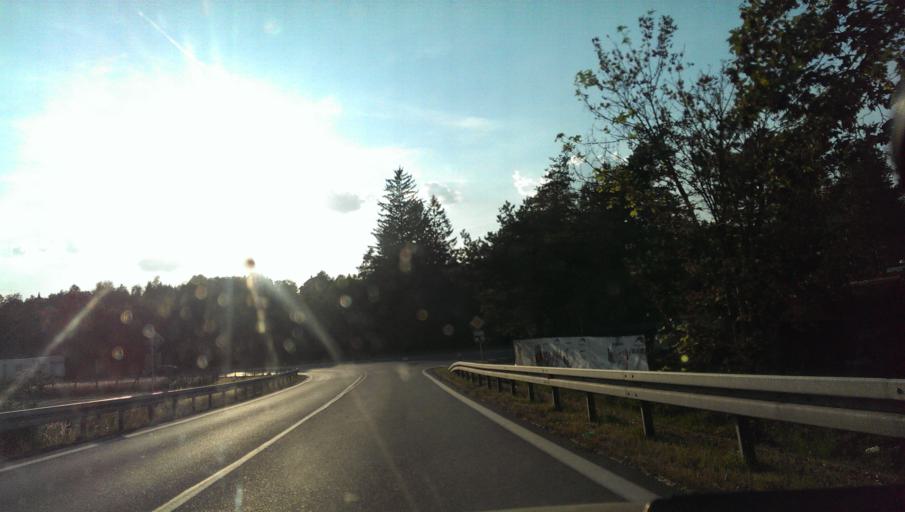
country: CZ
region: Zlin
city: Slusovice
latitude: 49.2114
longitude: 17.8136
